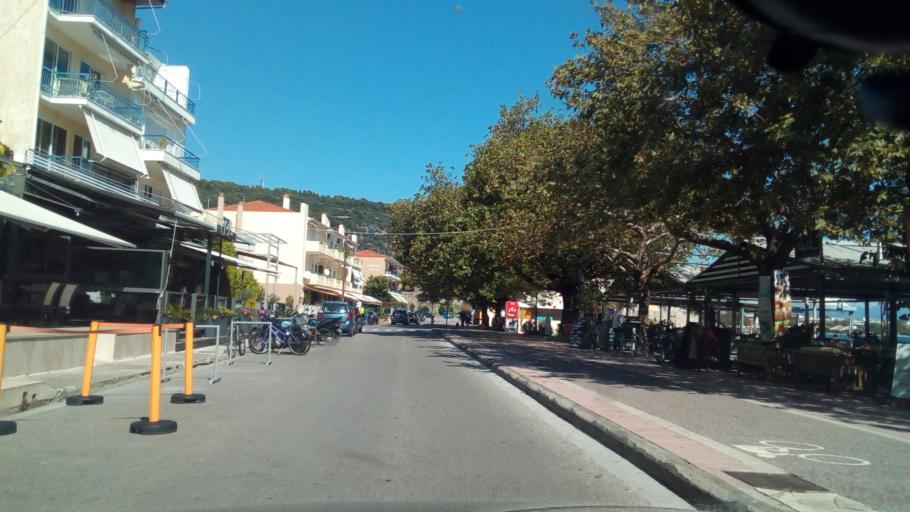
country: GR
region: West Greece
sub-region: Nomos Aitolias kai Akarnanias
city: Nafpaktos
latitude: 38.3912
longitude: 21.8254
